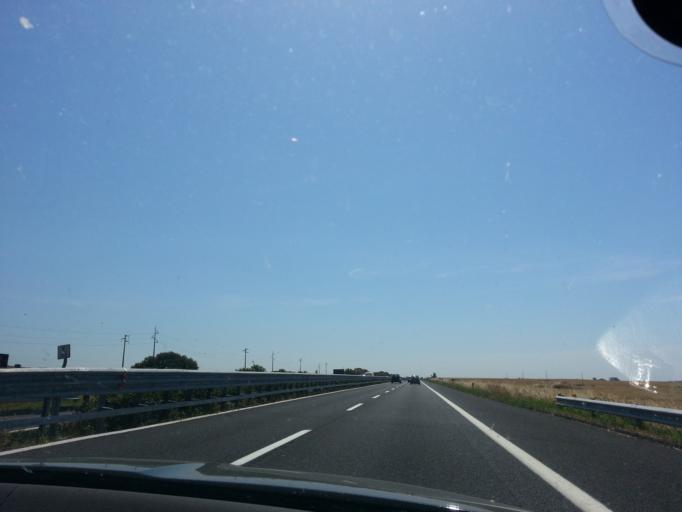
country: IT
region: Latium
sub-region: Citta metropolitana di Roma Capitale
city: Marina di Cerveteri
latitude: 42.0179
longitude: 12.0035
